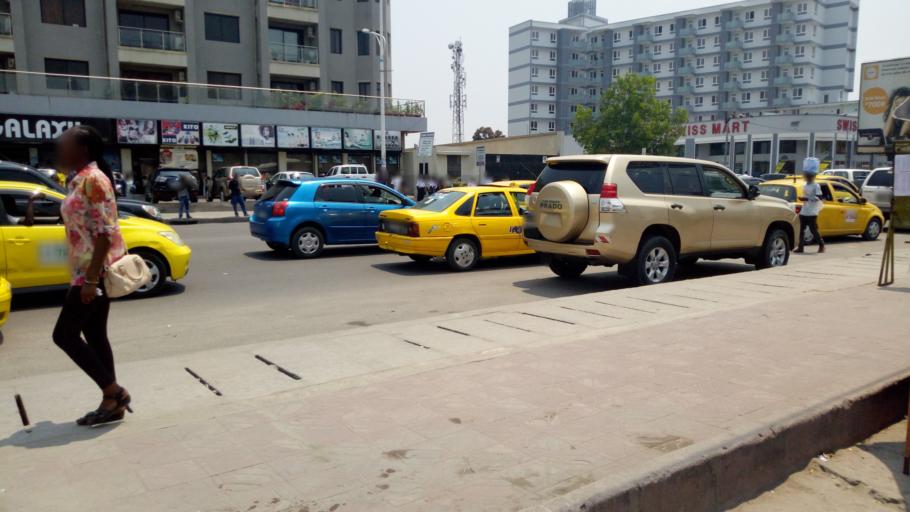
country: CD
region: Kinshasa
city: Kinshasa
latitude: -4.3174
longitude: 15.2924
